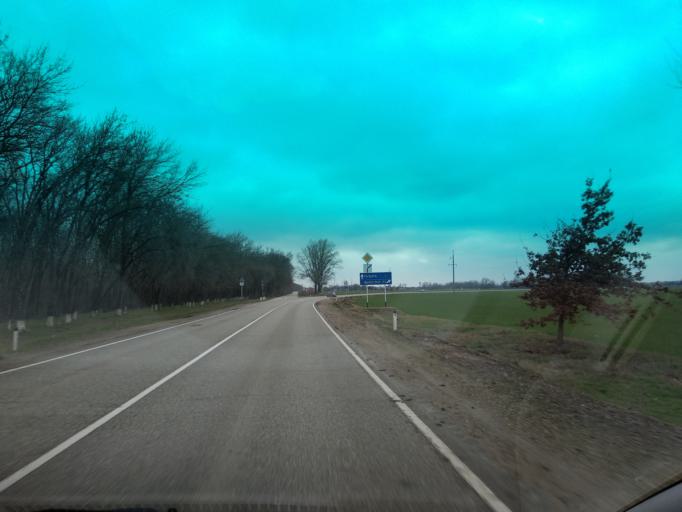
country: RU
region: Krasnodarskiy
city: Novorozhdestvenskaya
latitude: 45.7709
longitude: 39.9589
